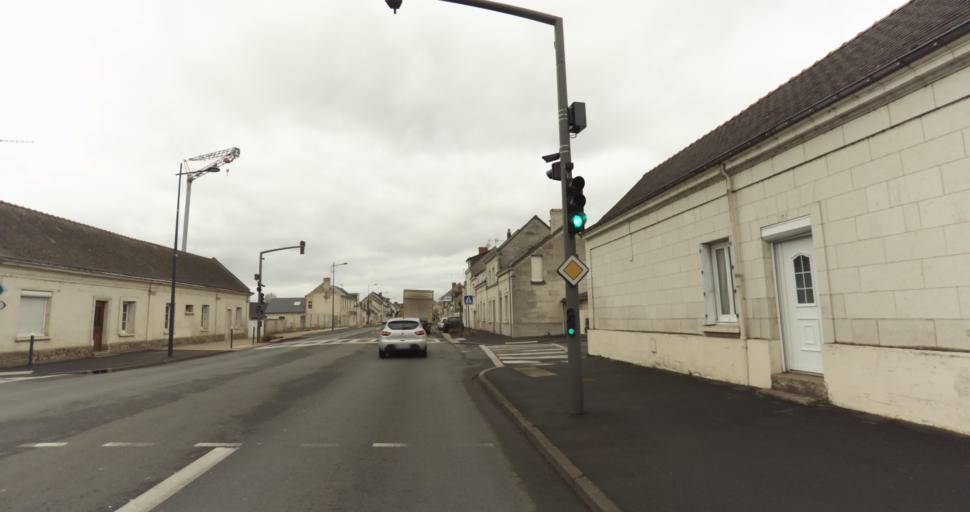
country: FR
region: Pays de la Loire
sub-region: Departement de Maine-et-Loire
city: Vivy
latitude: 47.3239
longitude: -0.0540
